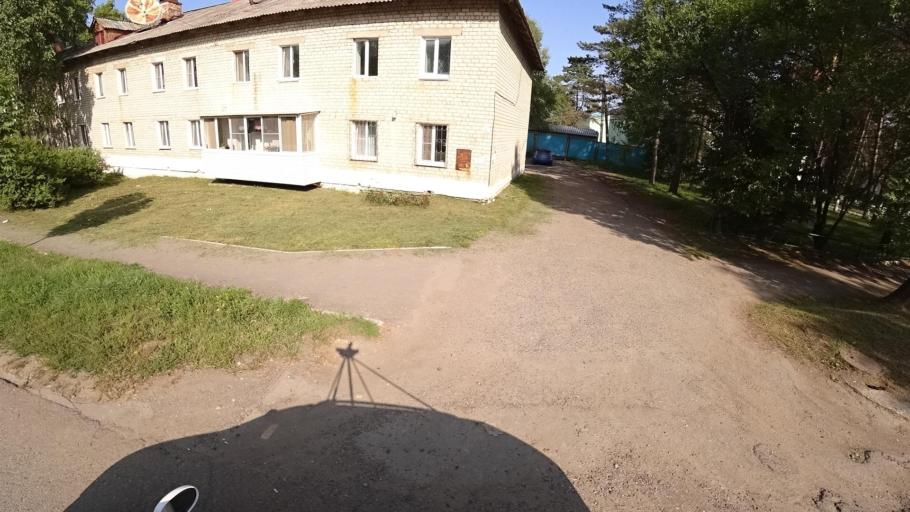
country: RU
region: Khabarovsk Krai
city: Khor
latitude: 47.9696
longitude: 135.0519
